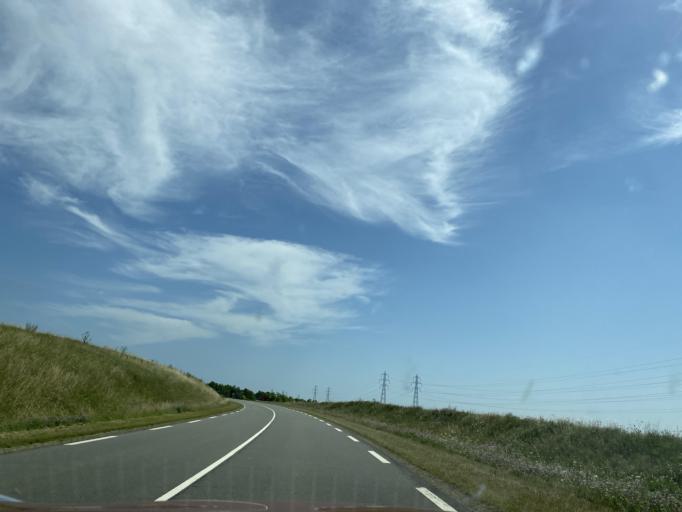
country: FR
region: Centre
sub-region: Departement d'Eure-et-Loir
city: Baigneaux
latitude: 48.1328
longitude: 1.8511
